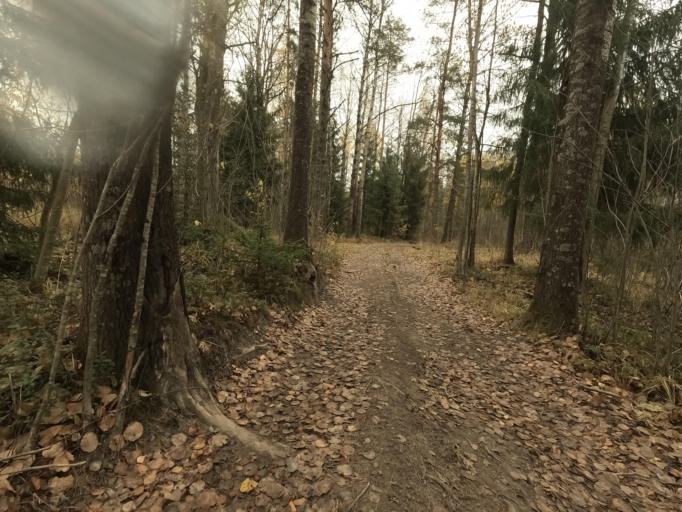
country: RU
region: Leningrad
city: Pavlovo
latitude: 59.7708
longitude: 30.9129
